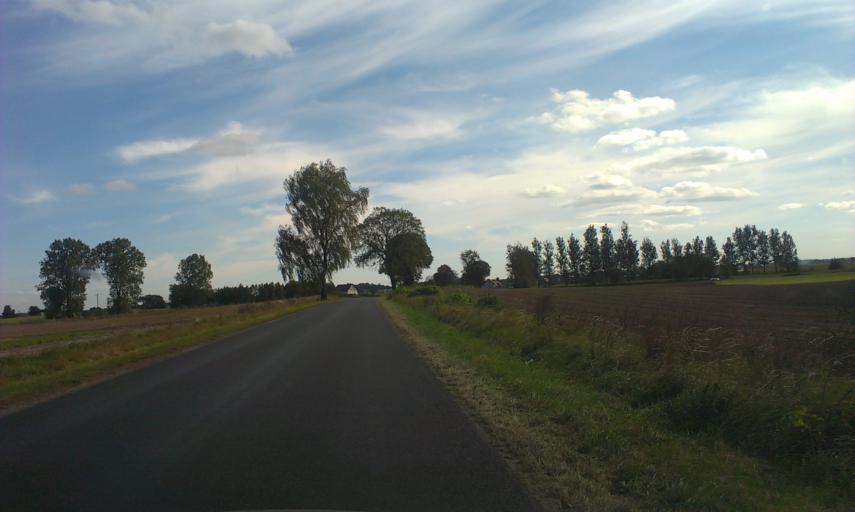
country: PL
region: Greater Poland Voivodeship
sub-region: Powiat zlotowski
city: Zlotow
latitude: 53.3130
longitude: 17.1200
